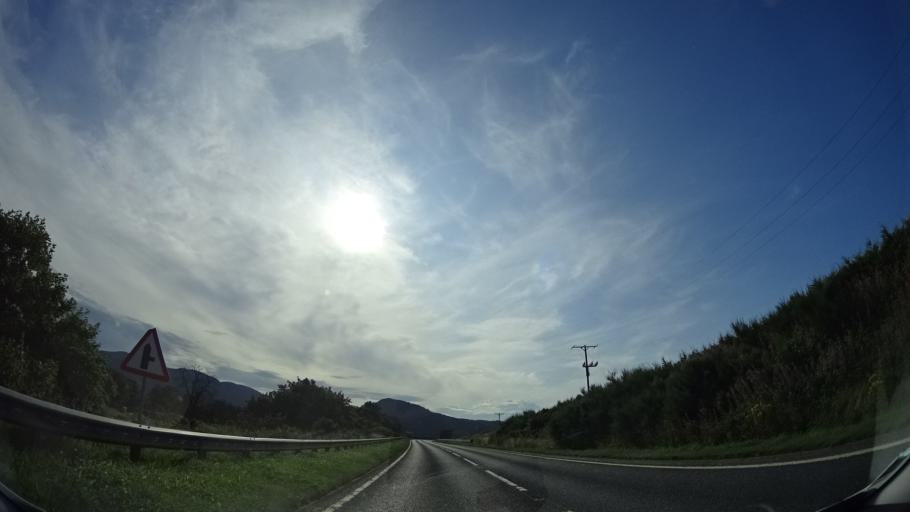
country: GB
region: Scotland
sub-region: Highland
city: Muir of Ord
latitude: 57.5611
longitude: -4.5567
